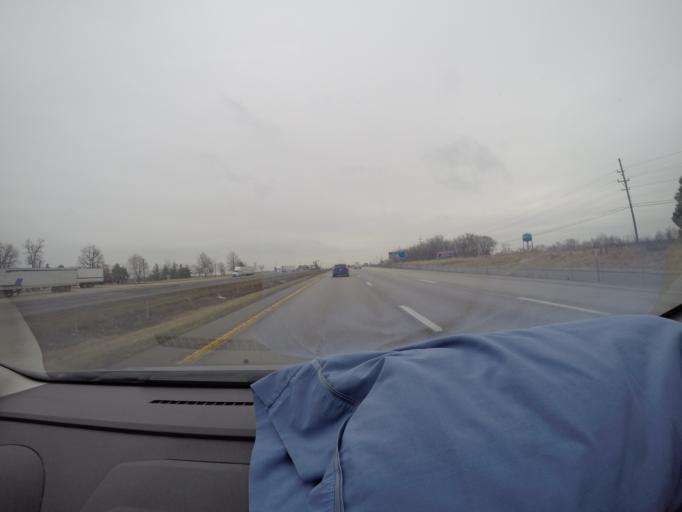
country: US
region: Missouri
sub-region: Warren County
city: Wright City
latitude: 38.8281
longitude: -91.0506
